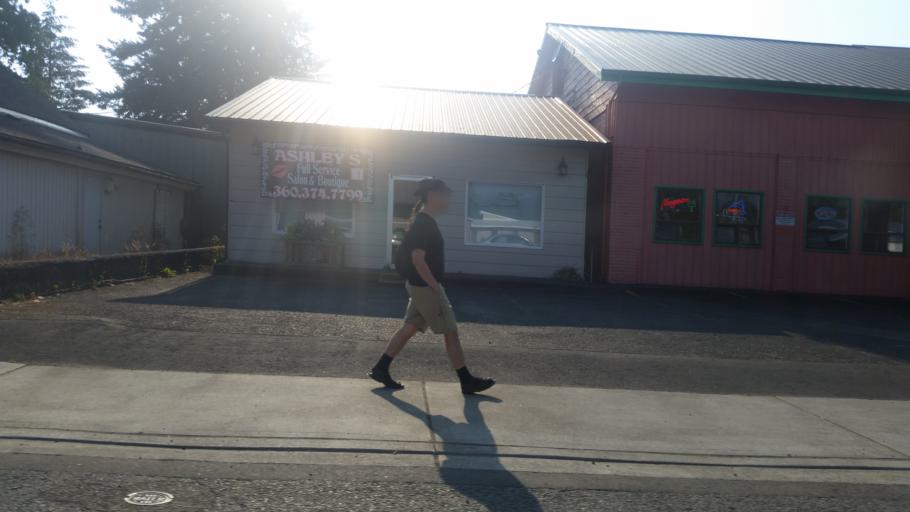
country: US
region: Washington
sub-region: Clallam County
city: Forks
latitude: 47.9513
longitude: -124.3855
